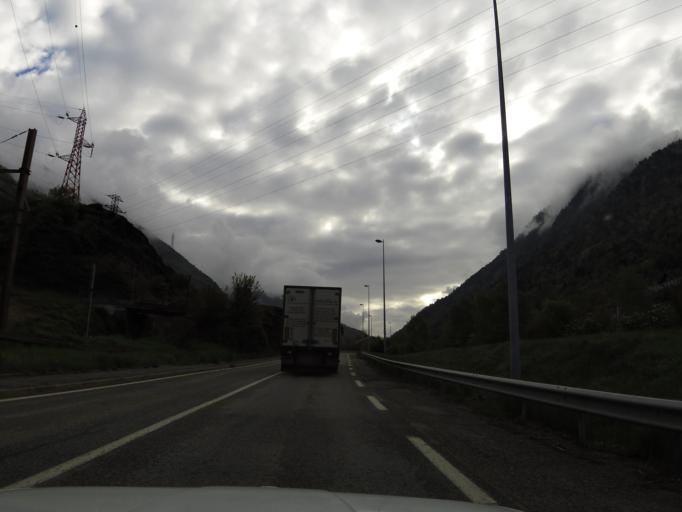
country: FR
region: Rhone-Alpes
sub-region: Departement de la Savoie
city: Saint-Michel-de-Maurienne
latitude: 45.2107
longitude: 6.4825
